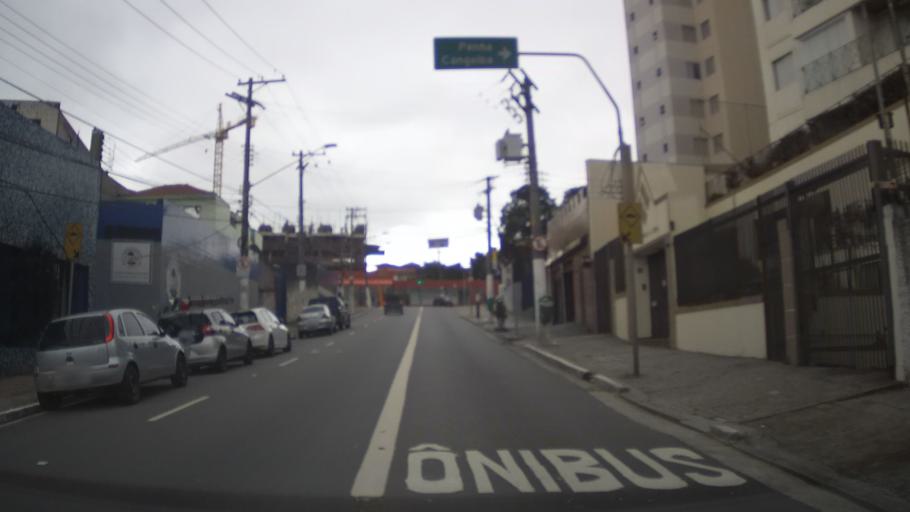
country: BR
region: Sao Paulo
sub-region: Guarulhos
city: Guarulhos
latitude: -23.5235
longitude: -46.5252
